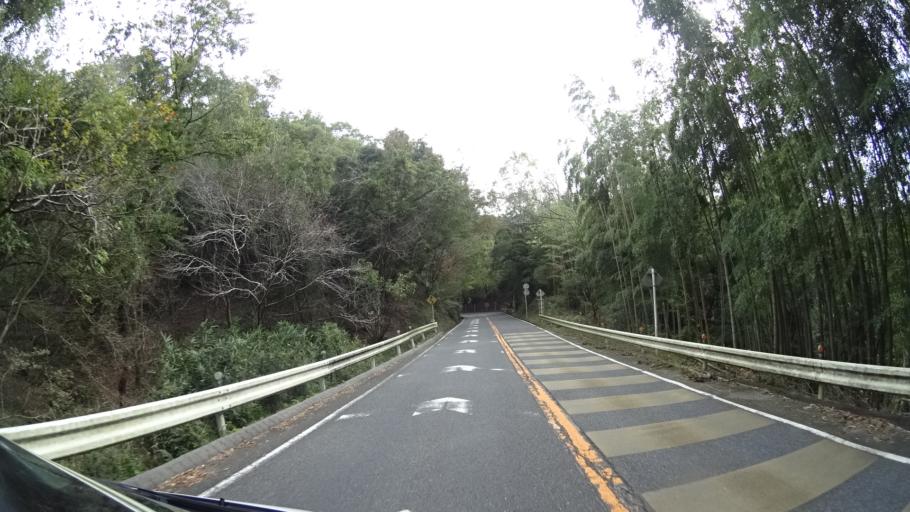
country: JP
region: Shiga Prefecture
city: Otsu-shi
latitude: 35.0428
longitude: 135.8210
